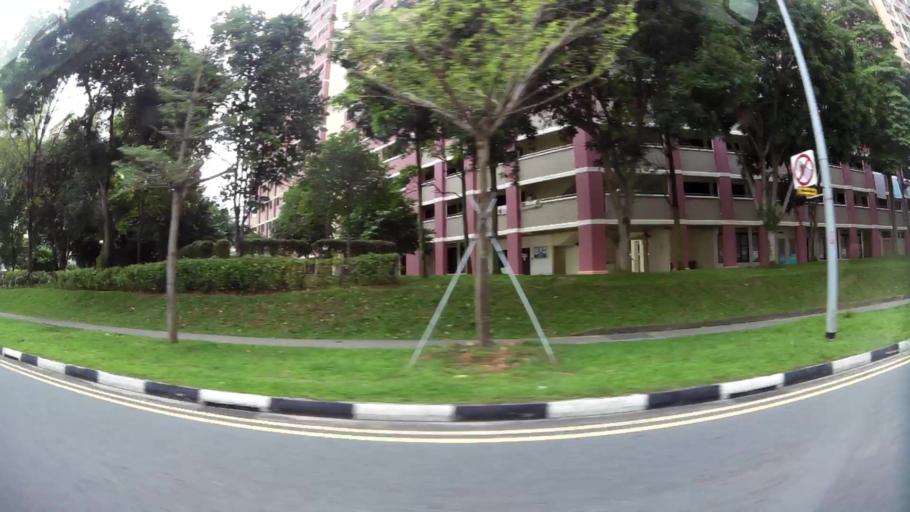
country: SG
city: Singapore
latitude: 1.3603
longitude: 103.9374
